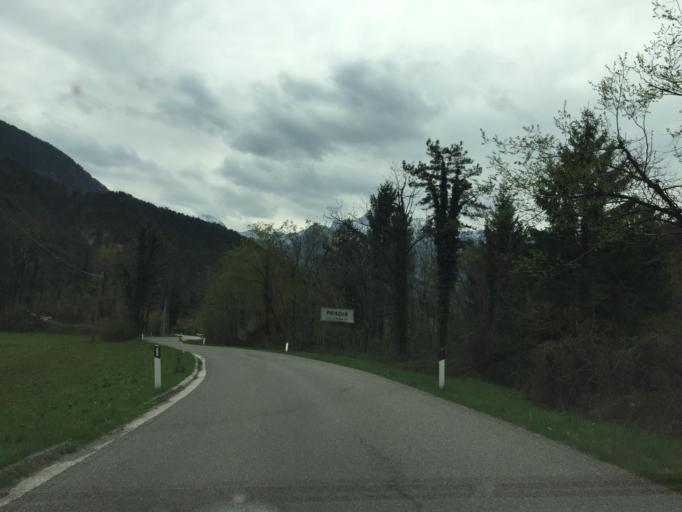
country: IT
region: Friuli Venezia Giulia
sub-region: Provincia di Udine
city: Moggio Udinese
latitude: 46.4274
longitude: 13.2020
